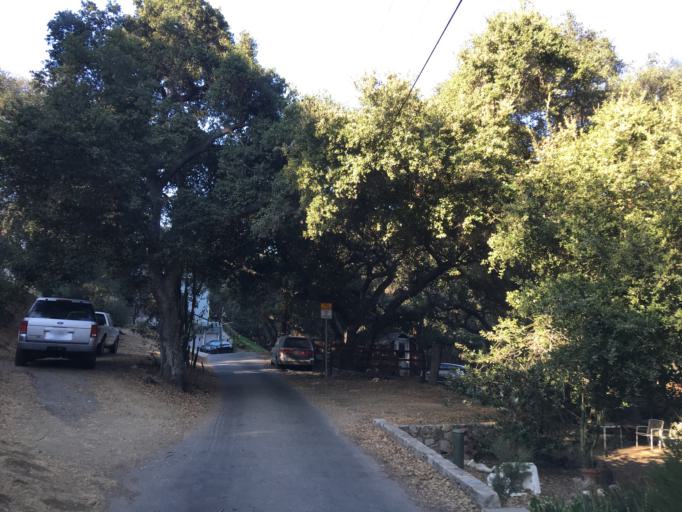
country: US
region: California
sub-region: Los Angeles County
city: San Fernando
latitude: 34.2931
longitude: -118.3757
